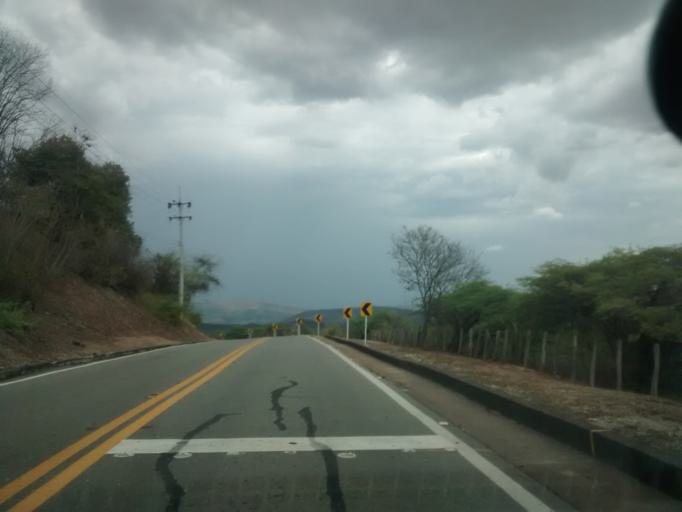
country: CO
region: Cundinamarca
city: Agua de Dios
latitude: 4.4039
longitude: -74.7271
